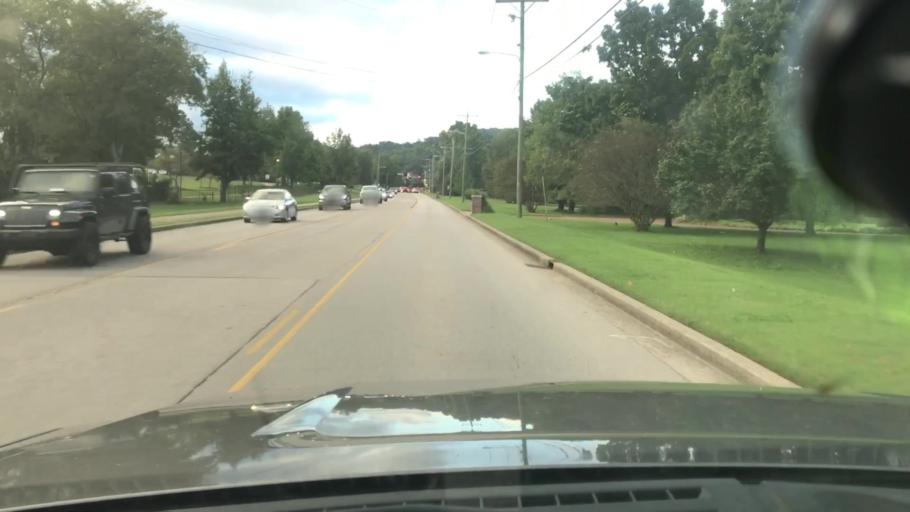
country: US
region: Tennessee
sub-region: Williamson County
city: Brentwood
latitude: 36.0221
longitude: -86.8204
